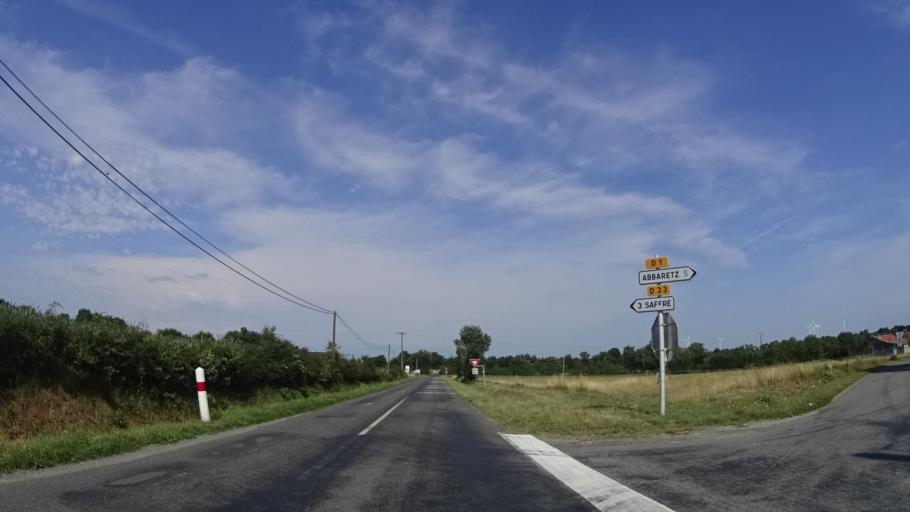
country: FR
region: Pays de la Loire
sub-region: Departement de la Loire-Atlantique
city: Saffre
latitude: 47.5127
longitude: -1.5452
